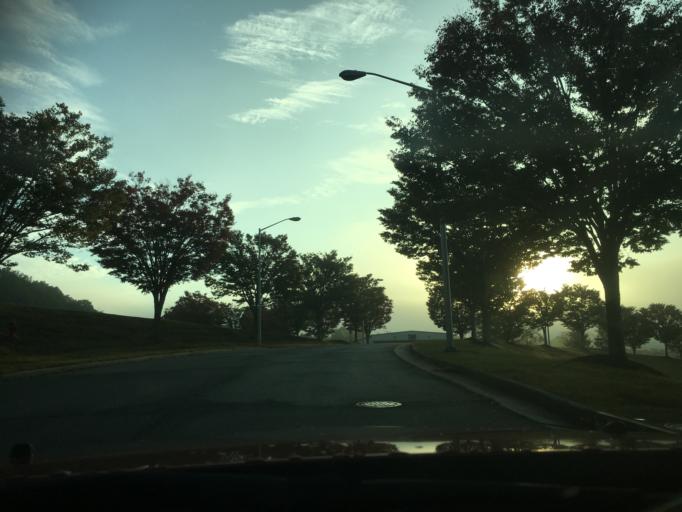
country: US
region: Virginia
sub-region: City of Radford
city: Radford
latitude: 37.0962
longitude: -80.5766
